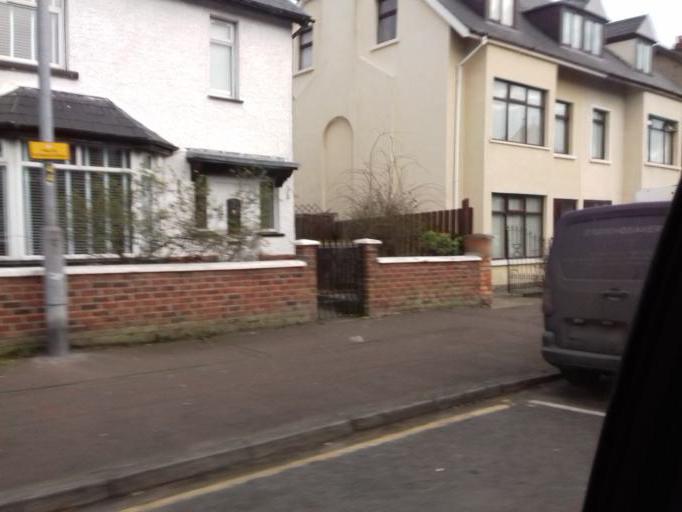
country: GB
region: Northern Ireland
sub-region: City of Belfast
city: Belfast
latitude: 54.6206
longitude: -5.9540
